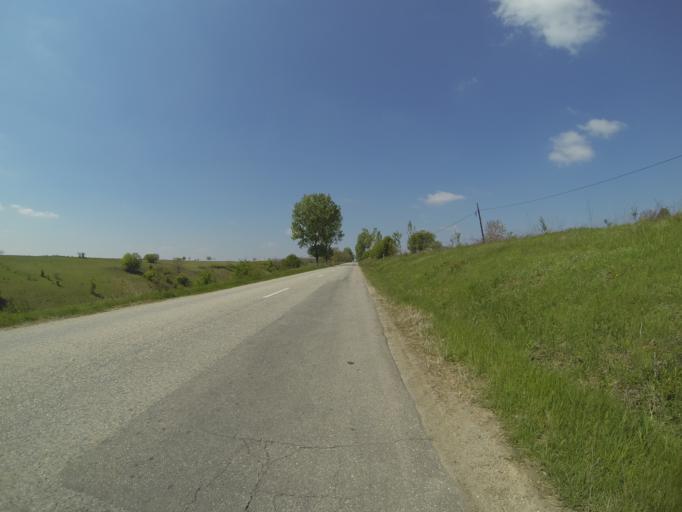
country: RO
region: Dolj
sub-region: Comuna Terpezita
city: Terpezita
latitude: 44.2914
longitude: 23.5328
